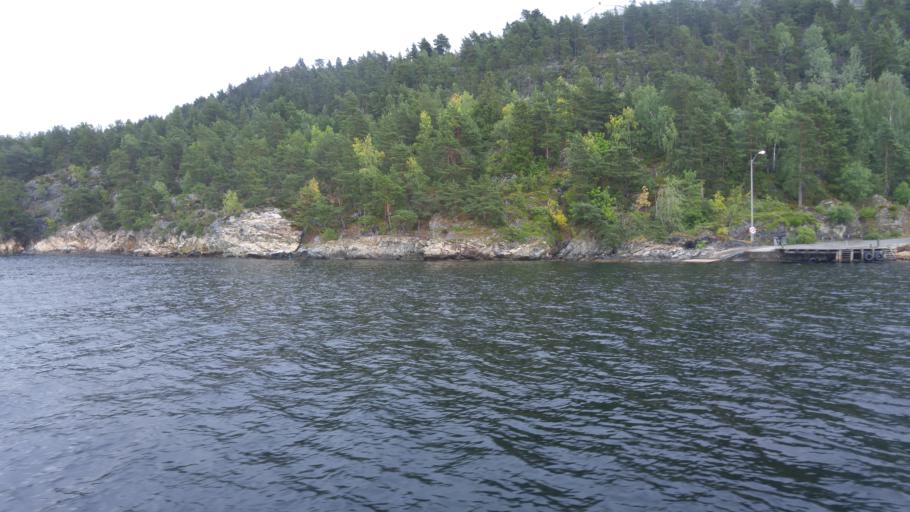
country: NO
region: Akershus
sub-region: Nesodden
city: Nesoddtangen
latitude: 59.8188
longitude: 10.6165
